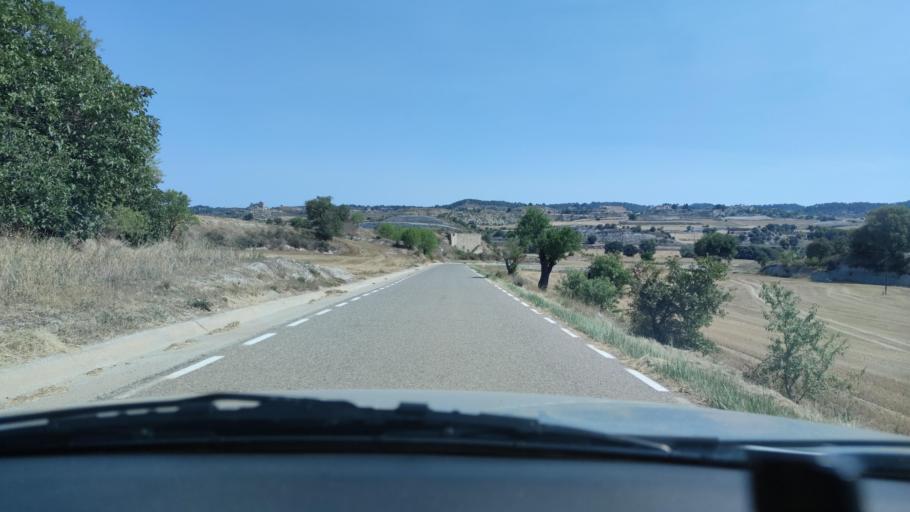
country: ES
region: Catalonia
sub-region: Provincia de Lleida
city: Cervera
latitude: 41.6304
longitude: 1.3286
